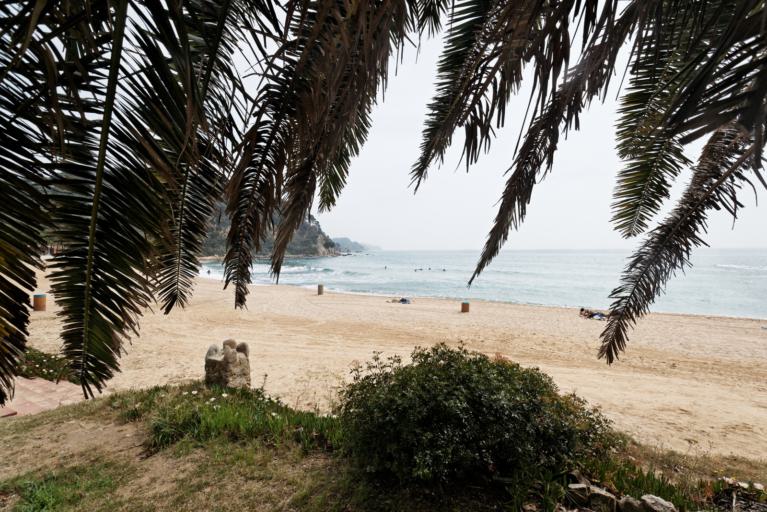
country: ES
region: Catalonia
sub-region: Provincia de Girona
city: Blanes
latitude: 41.6876
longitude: 2.8175
